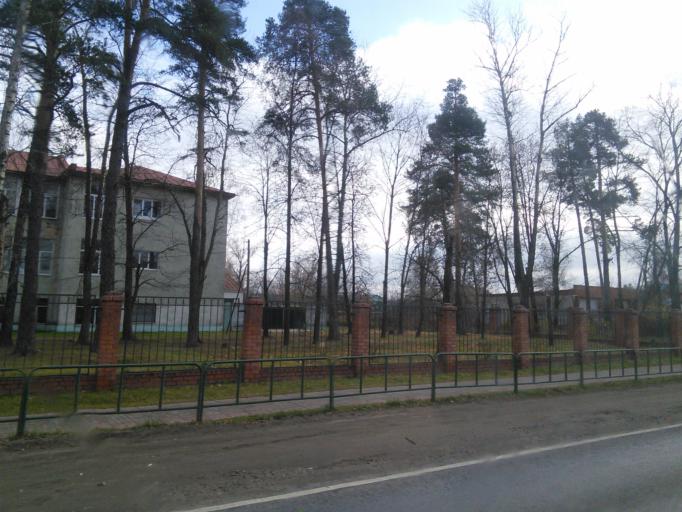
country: RU
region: Moskovskaya
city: Likino-Dulevo
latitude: 55.7110
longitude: 38.9578
